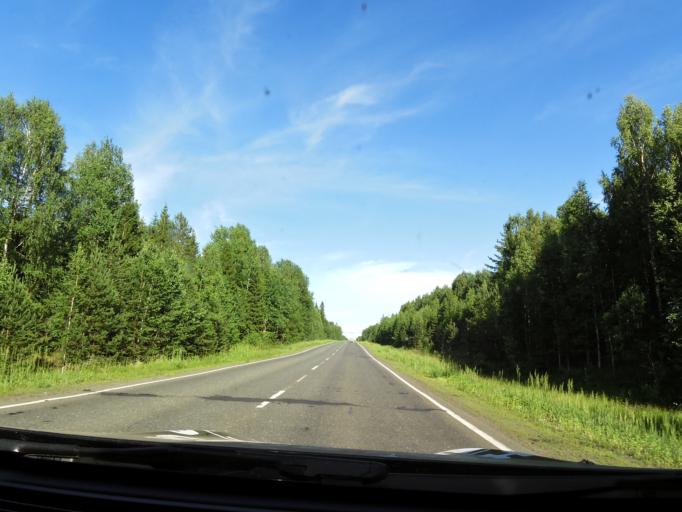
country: RU
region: Kirov
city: Chernaya Kholunitsa
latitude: 58.8869
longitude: 51.3847
